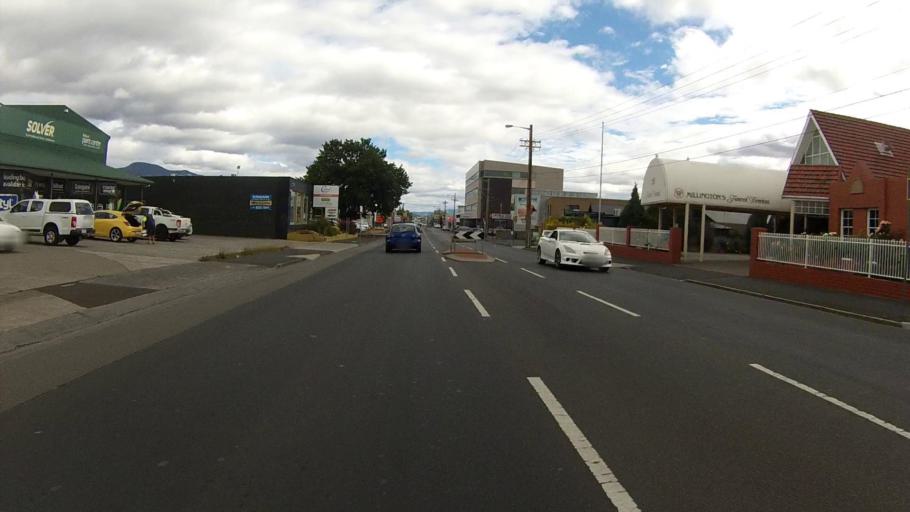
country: AU
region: Tasmania
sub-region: Glenorchy
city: Moonah
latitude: -42.8439
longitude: 147.2928
